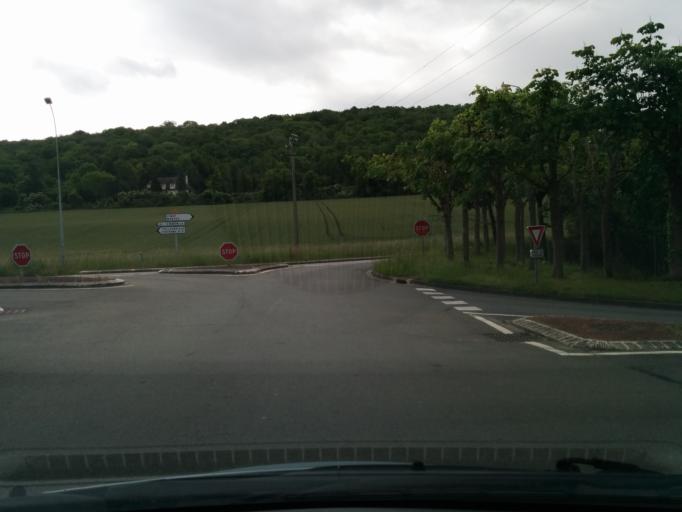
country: FR
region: Ile-de-France
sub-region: Departement des Yvelines
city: Follainville-Dennemont
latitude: 49.0189
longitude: 1.6966
